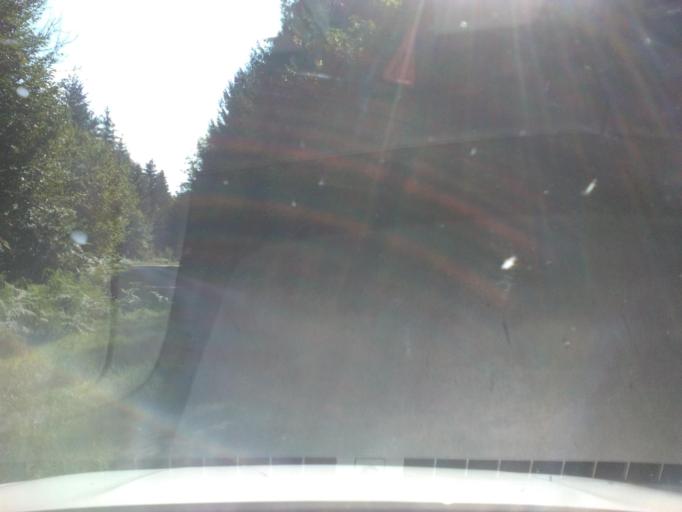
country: FR
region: Lorraine
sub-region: Departement des Vosges
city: Ban-de-Laveline
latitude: 48.3286
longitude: 7.0602
